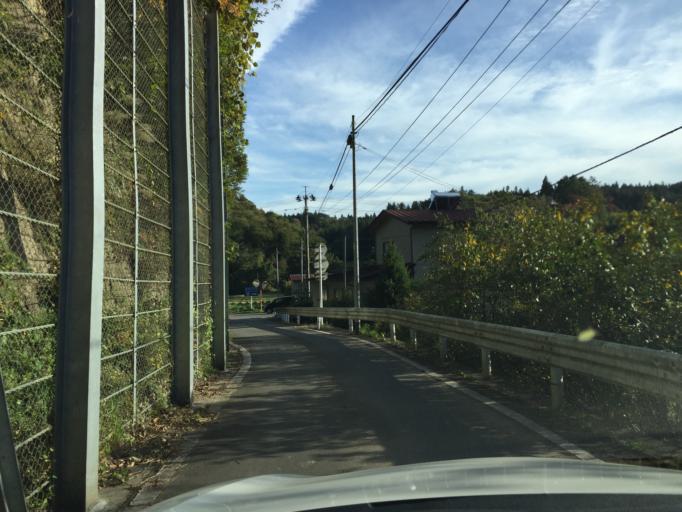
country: JP
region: Fukushima
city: Ishikawa
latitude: 37.2297
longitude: 140.6079
